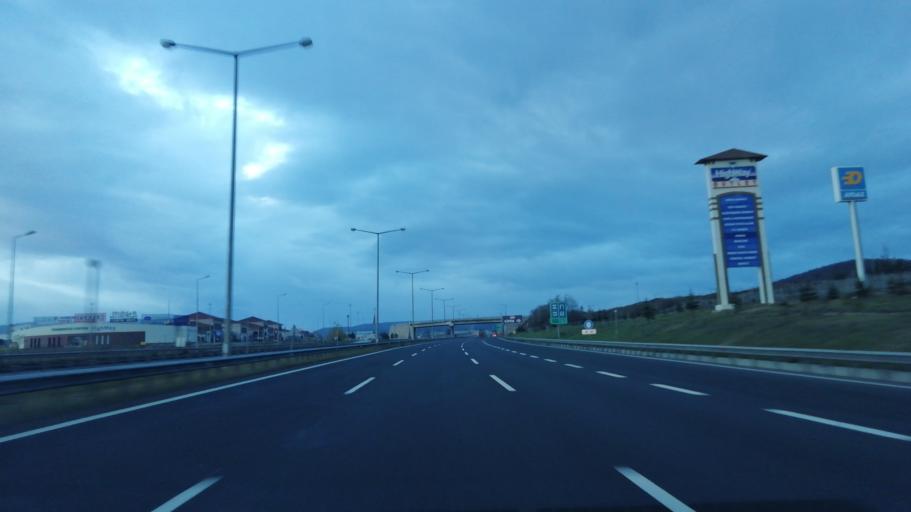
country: TR
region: Bolu
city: Bolu
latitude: 40.7225
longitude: 31.4726
